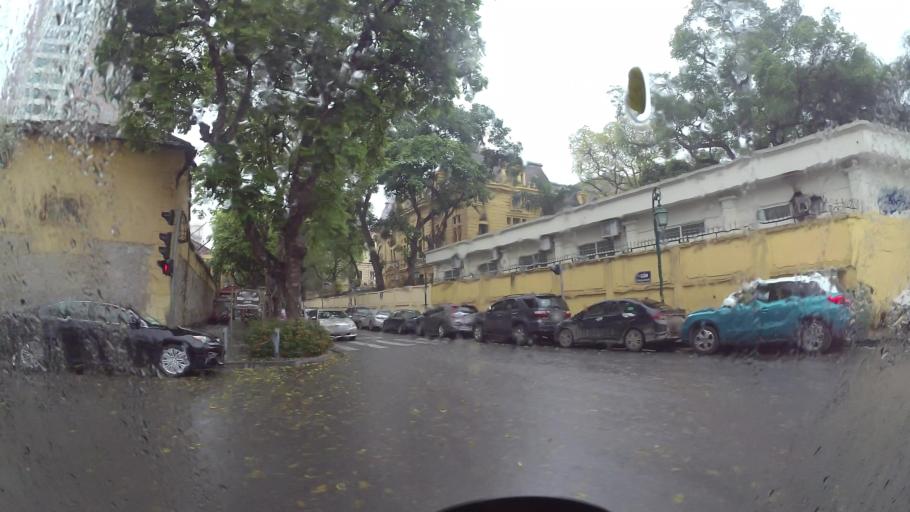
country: VN
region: Ha Noi
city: Hanoi
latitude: 21.0248
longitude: 105.8464
